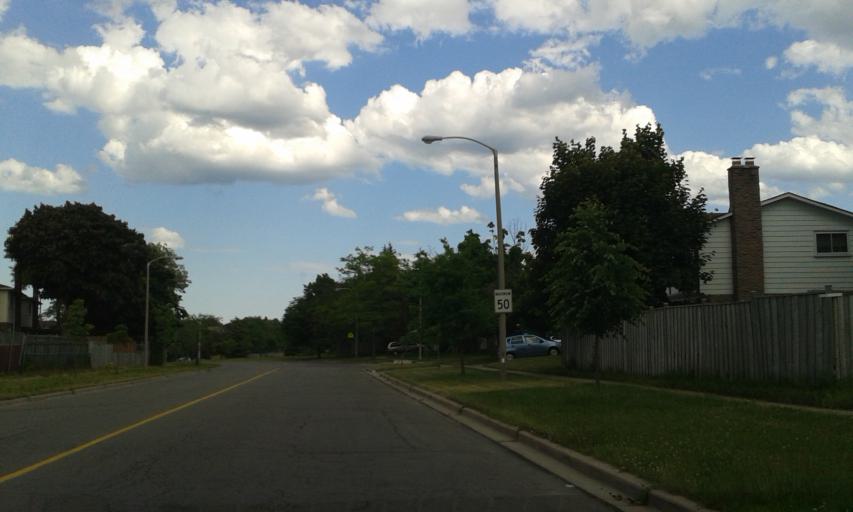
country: CA
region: Ontario
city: Scarborough
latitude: 43.8055
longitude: -79.2684
